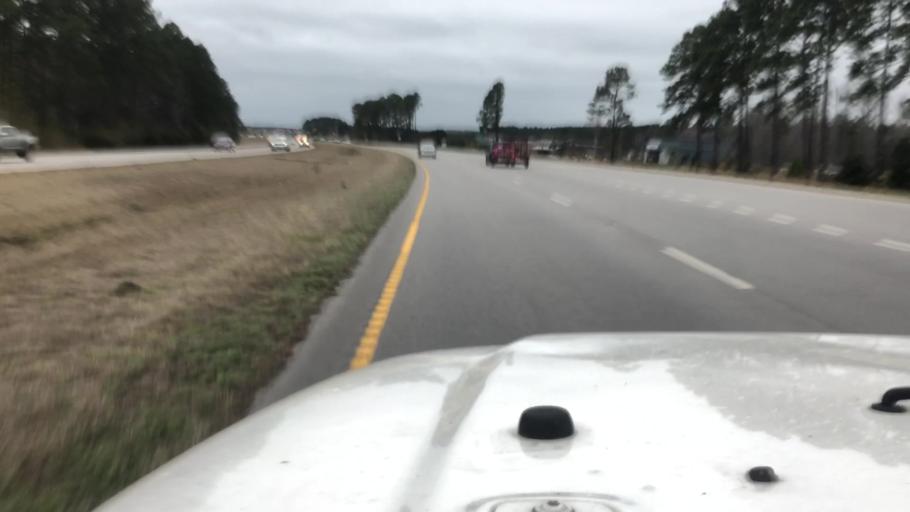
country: US
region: South Carolina
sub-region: Beaufort County
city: Bluffton
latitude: 32.2972
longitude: -80.9417
